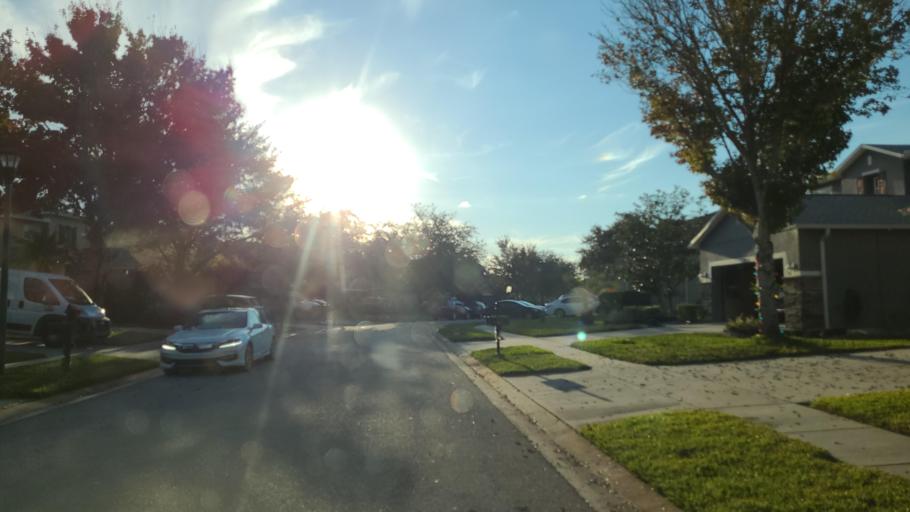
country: US
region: Florida
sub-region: Hillsborough County
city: Cheval
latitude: 28.2069
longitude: -82.5257
